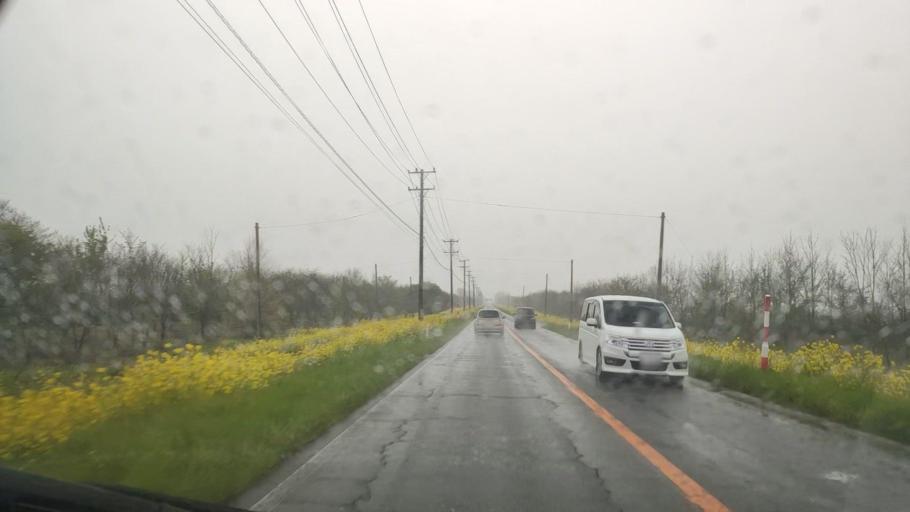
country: JP
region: Akita
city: Tenno
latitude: 39.9998
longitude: 139.9463
